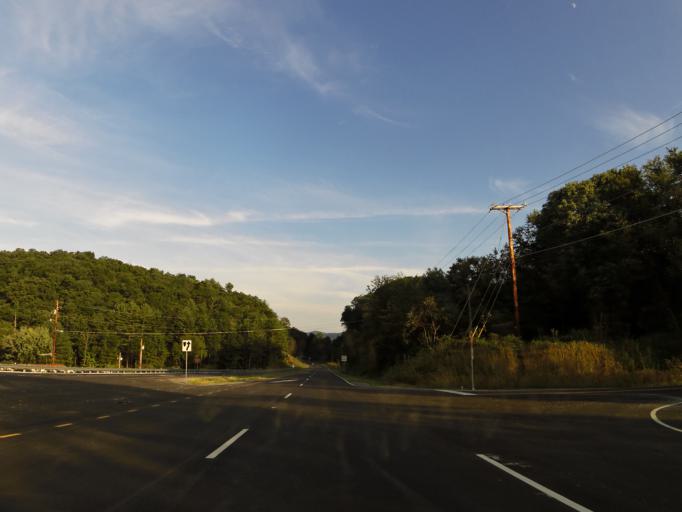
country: US
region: Virginia
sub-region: Washington County
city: Emory
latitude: 36.6628
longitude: -81.8569
